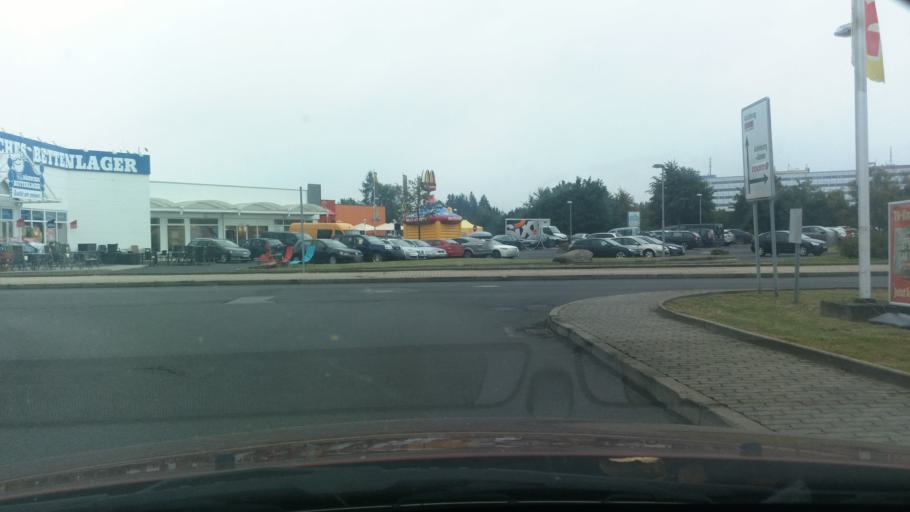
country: DE
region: Saxony
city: Goerlitz
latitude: 51.1696
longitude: 14.9678
